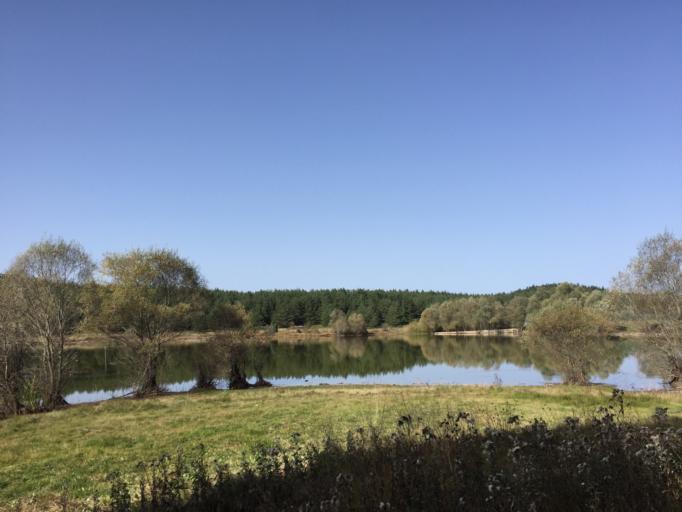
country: TR
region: Ankara
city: Pecenek
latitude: 40.6069
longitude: 32.2533
